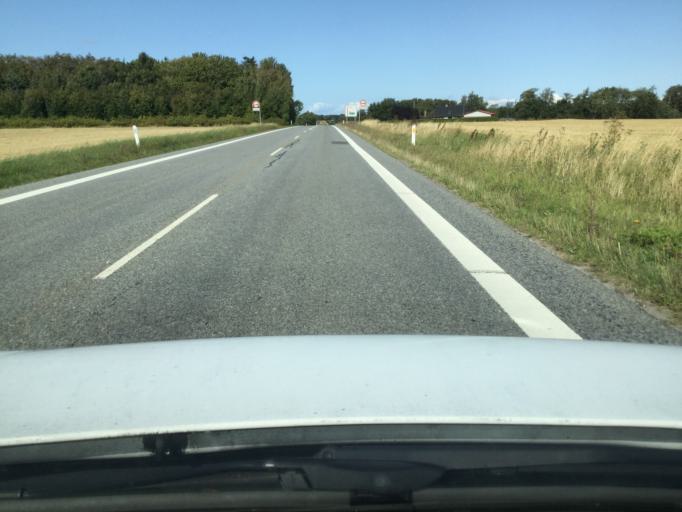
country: DK
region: Zealand
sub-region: Lolland Kommune
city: Rodby
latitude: 54.7191
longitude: 11.3839
